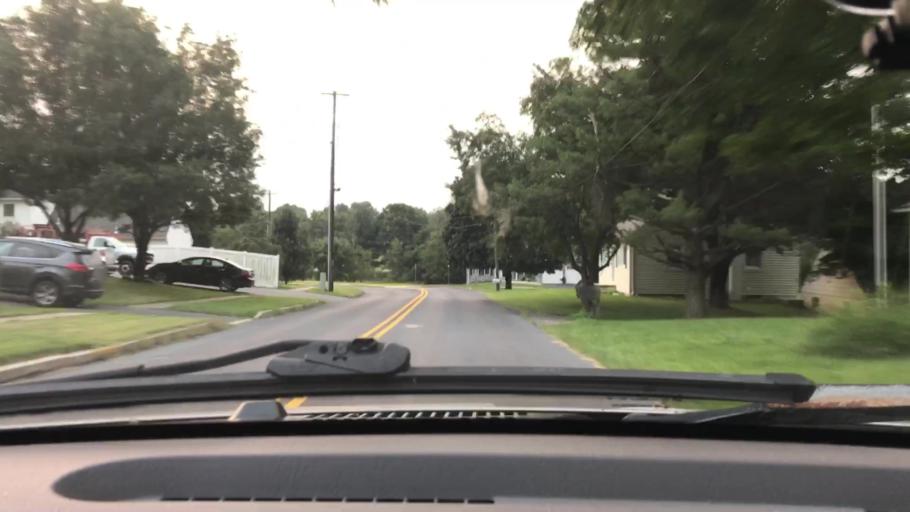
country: US
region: Pennsylvania
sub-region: Lancaster County
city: Elizabethtown
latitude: 40.1654
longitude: -76.5929
